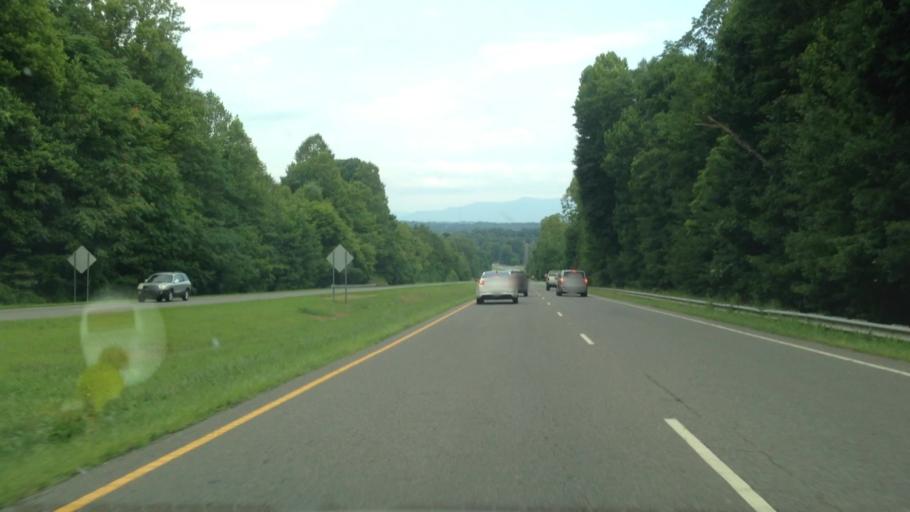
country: US
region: North Carolina
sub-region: Surry County
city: Mount Airy
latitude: 36.4759
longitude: -80.5866
